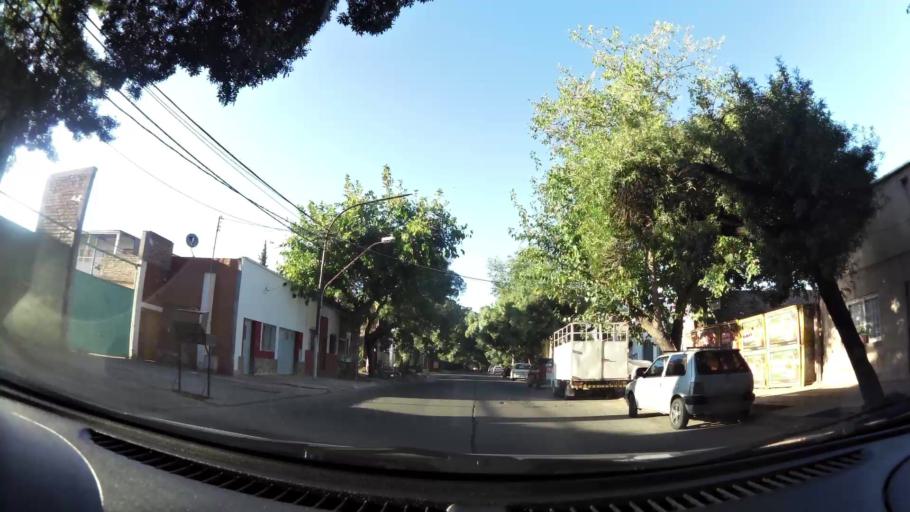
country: AR
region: Mendoza
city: Las Heras
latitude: -32.8688
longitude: -68.8291
